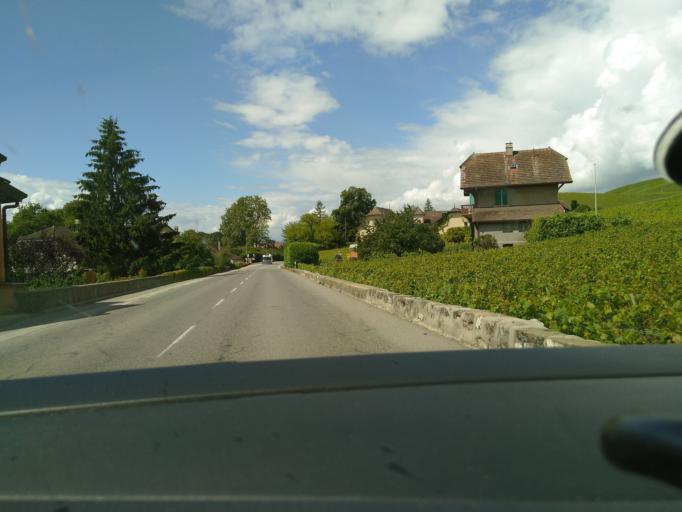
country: CH
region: Vaud
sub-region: Nyon District
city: Perroy
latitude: 46.4806
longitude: 6.3729
